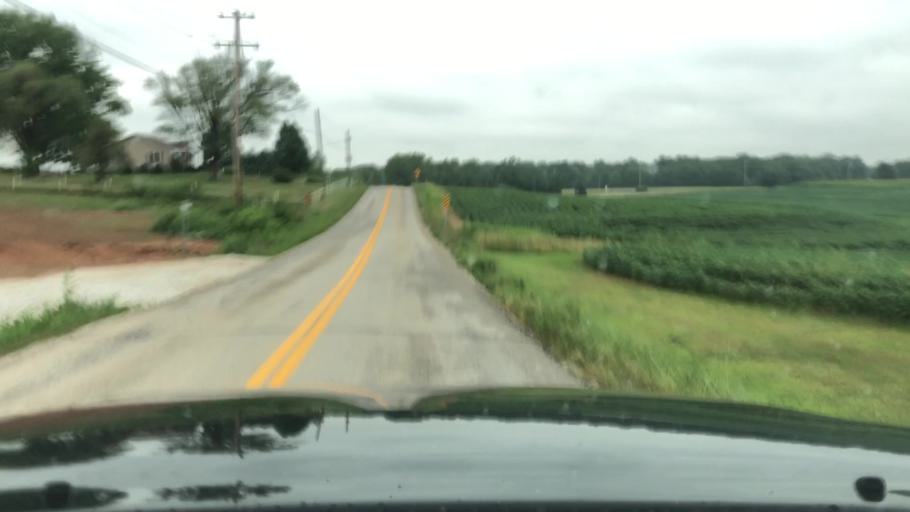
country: US
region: Missouri
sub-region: Saint Charles County
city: Wentzville
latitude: 38.8433
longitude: -90.8877
